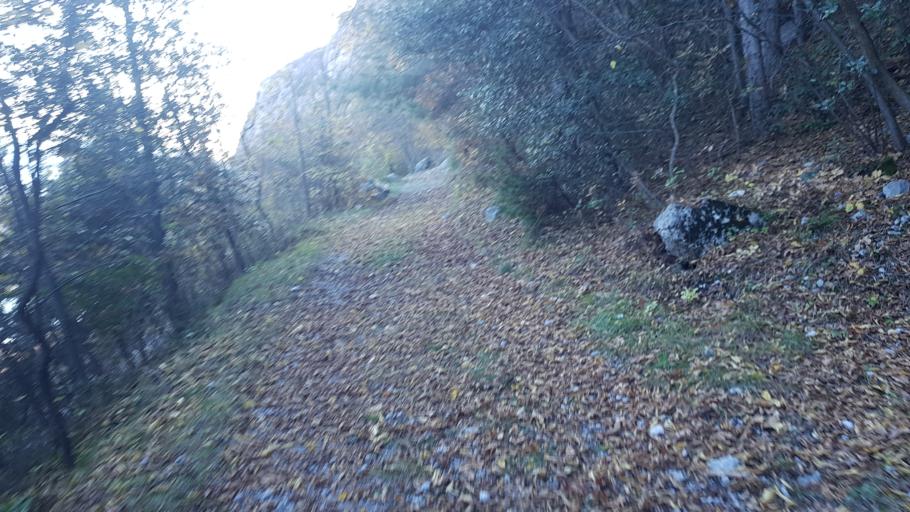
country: IT
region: Trentino-Alto Adige
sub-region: Provincia di Trento
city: Vezzano
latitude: 46.0764
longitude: 10.9817
